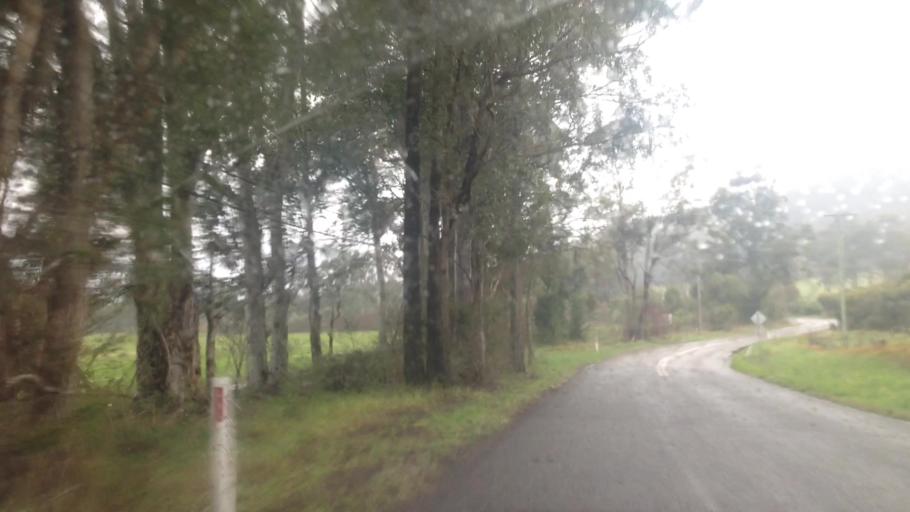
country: AU
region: New South Wales
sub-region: Wyong Shire
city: Little Jilliby
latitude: -33.2148
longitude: 151.3718
